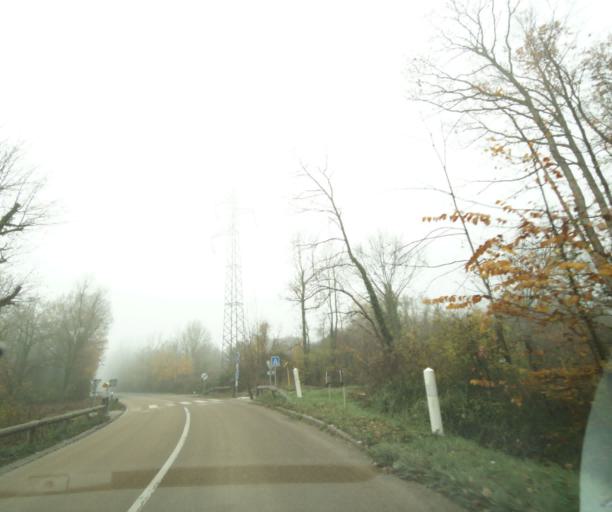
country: FR
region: Ile-de-France
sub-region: Departement de Seine-Saint-Denis
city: Clichy-sous-Bois
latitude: 48.9195
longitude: 2.5572
